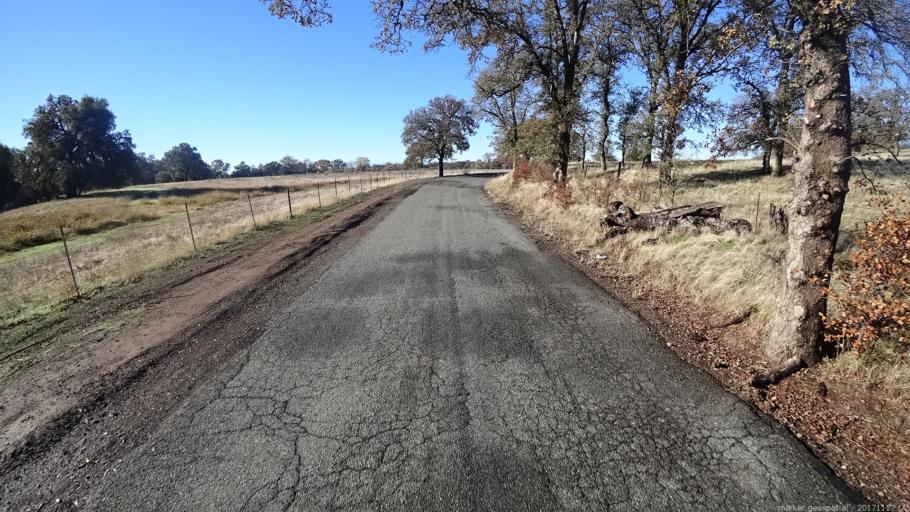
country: US
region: California
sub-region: Shasta County
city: Cottonwood
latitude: 40.4361
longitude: -122.1957
